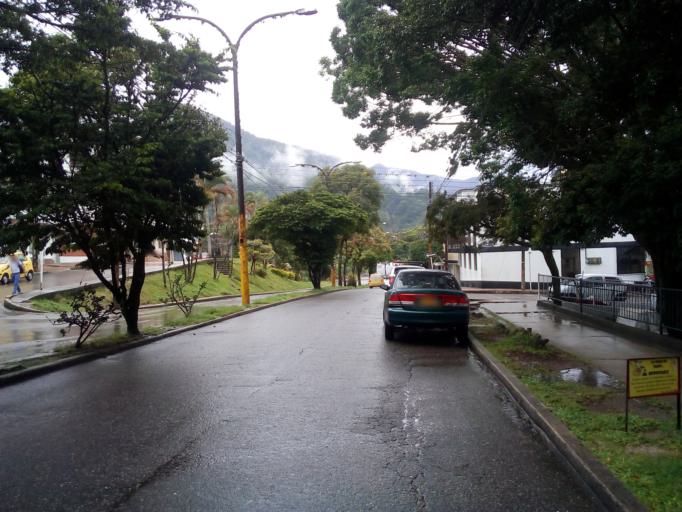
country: CO
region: Tolima
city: Ibague
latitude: 4.4481
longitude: -75.2439
